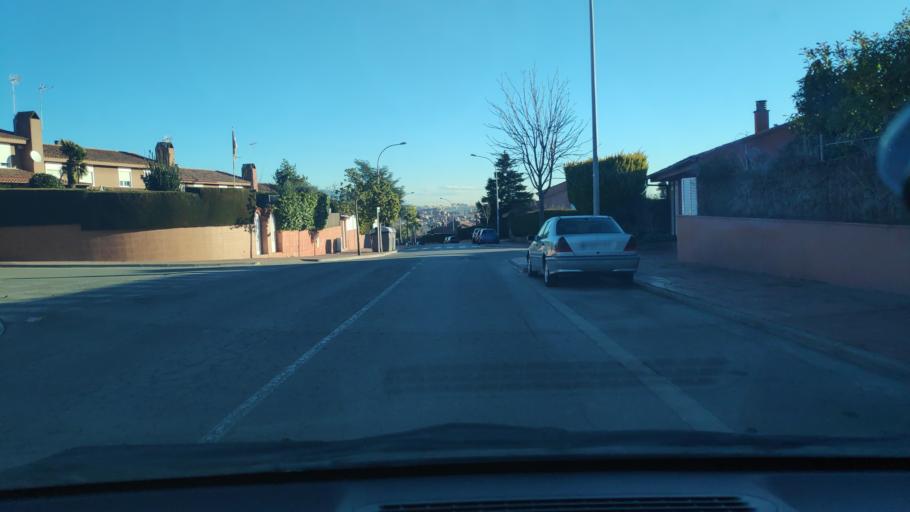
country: ES
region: Catalonia
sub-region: Provincia de Barcelona
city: Sant Quirze del Valles
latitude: 41.5272
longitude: 2.0730
